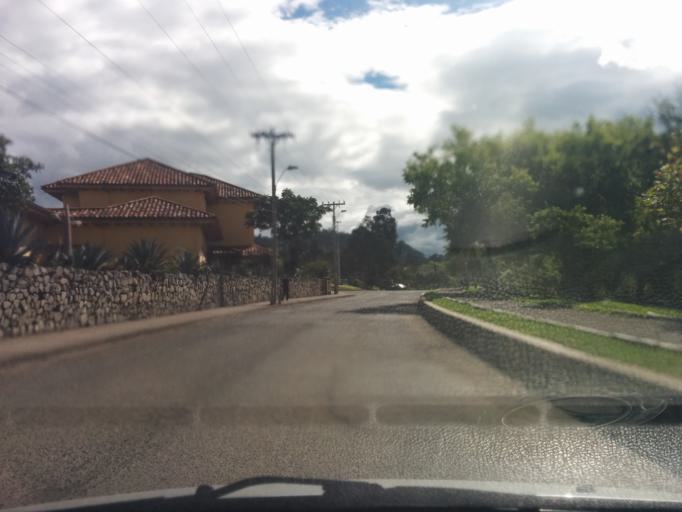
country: EC
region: Azuay
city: Cuenca
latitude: -2.9149
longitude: -78.9930
